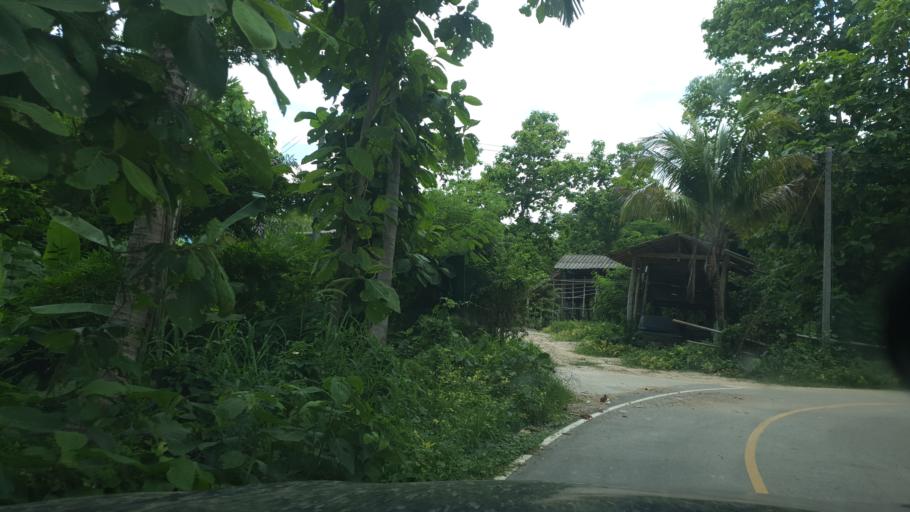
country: TH
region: Lampang
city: Sop Prap
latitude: 17.8690
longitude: 99.3876
